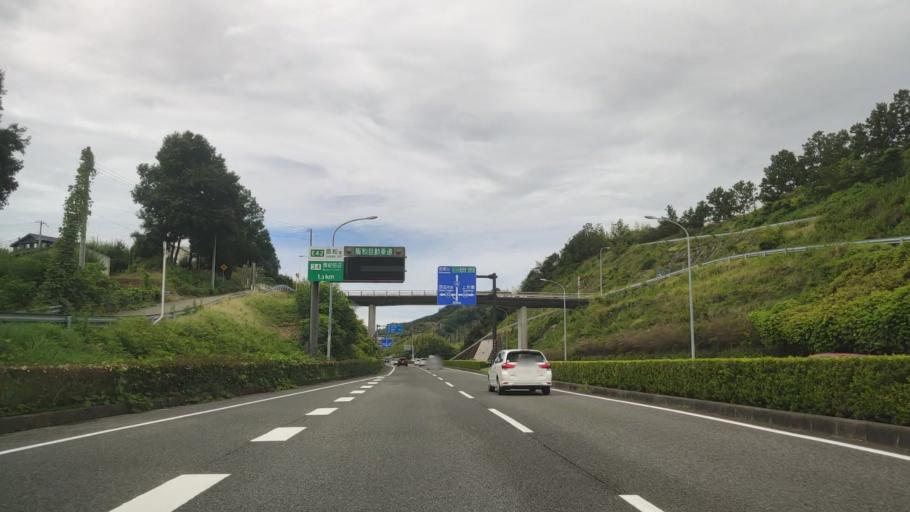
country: JP
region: Wakayama
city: Tanabe
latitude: 33.7446
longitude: 135.3823
